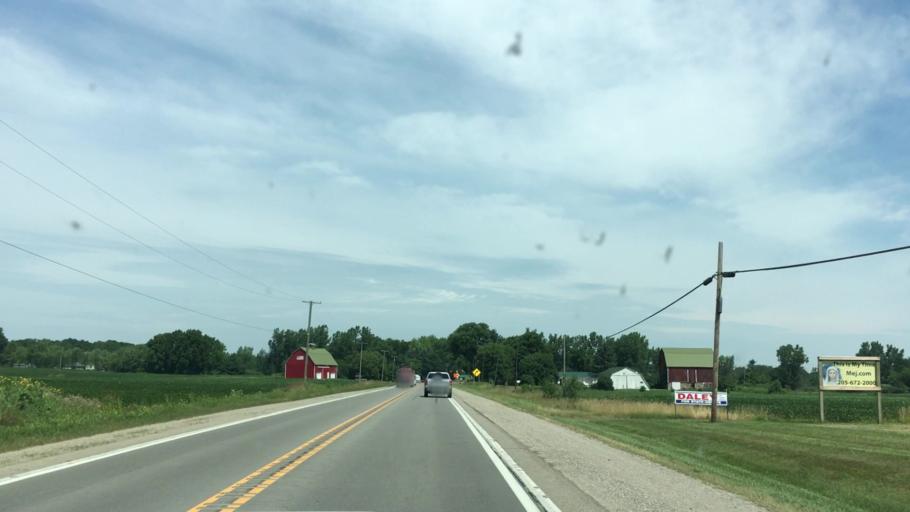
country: US
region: Michigan
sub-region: Lapeer County
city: Imlay City
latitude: 43.0619
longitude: -83.0721
